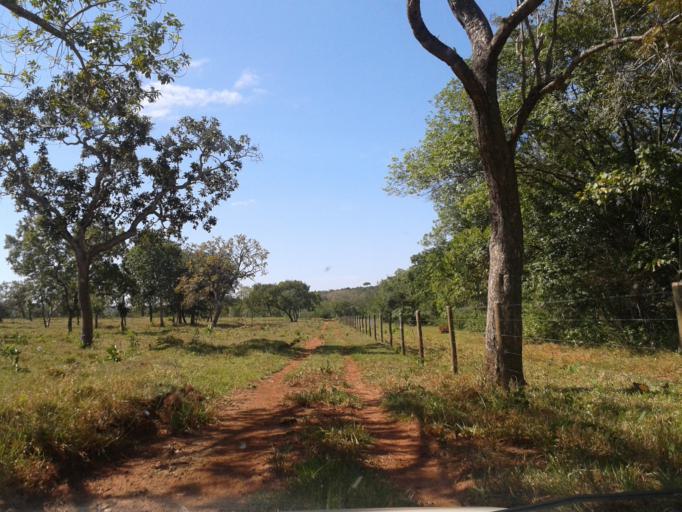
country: BR
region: Minas Gerais
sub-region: Campina Verde
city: Campina Verde
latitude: -19.4022
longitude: -49.7455
